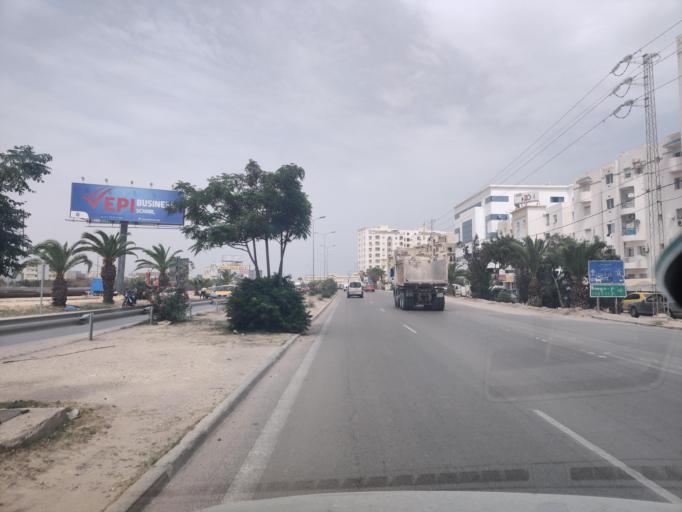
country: TN
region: Susah
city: Hammam Sousse
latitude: 35.8306
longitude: 10.5905
